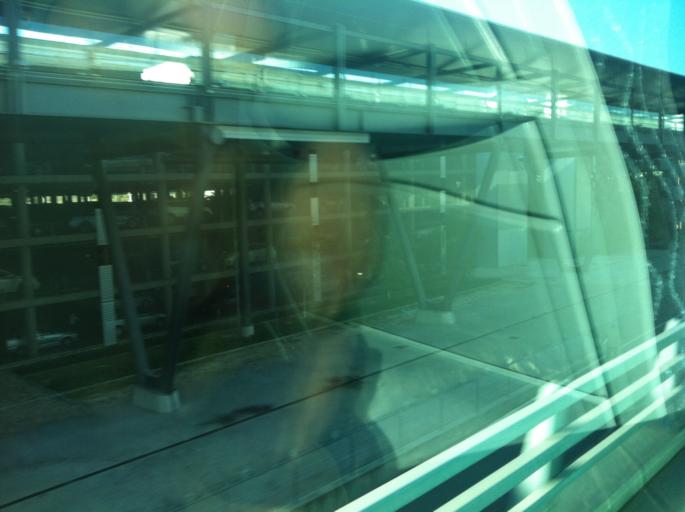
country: ES
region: Madrid
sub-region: Provincia de Madrid
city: Barajas de Madrid
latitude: 40.4929
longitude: -3.5942
